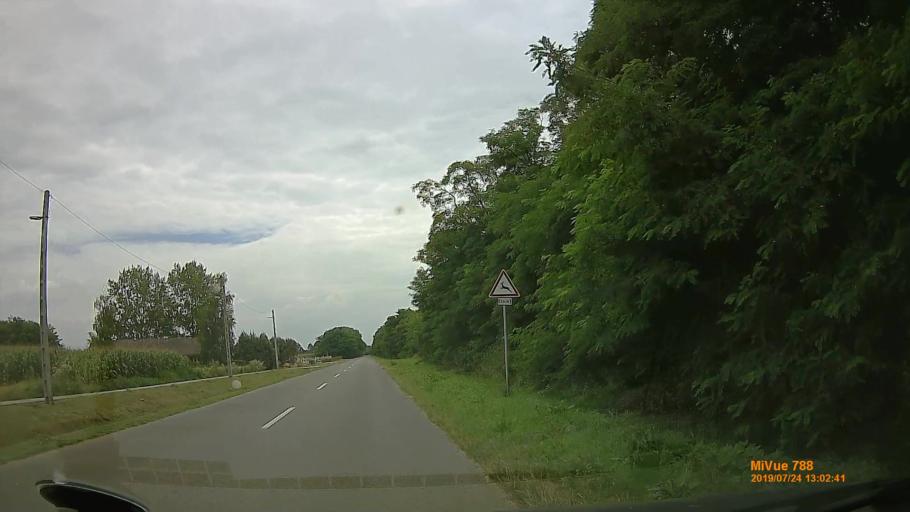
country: HU
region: Szabolcs-Szatmar-Bereg
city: Aranyosapati
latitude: 48.2205
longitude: 22.2948
